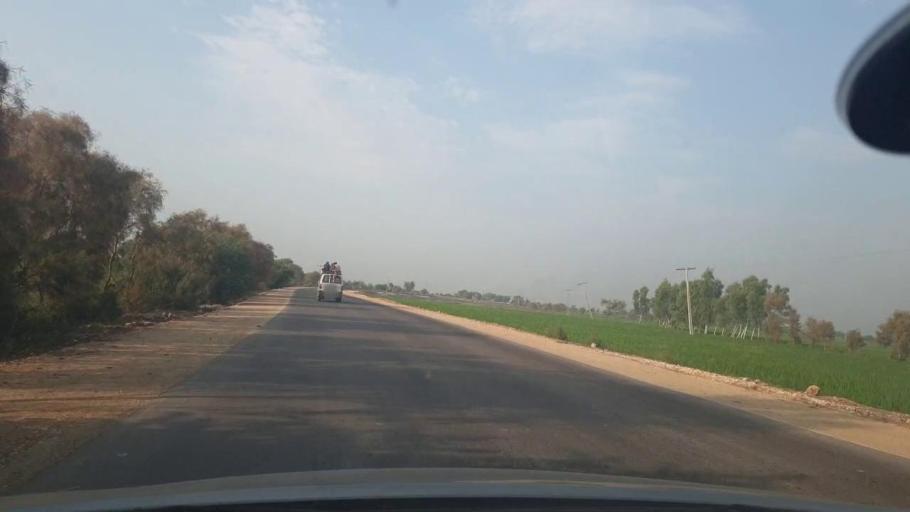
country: PK
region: Sindh
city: Jacobabad
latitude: 28.2403
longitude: 68.3923
